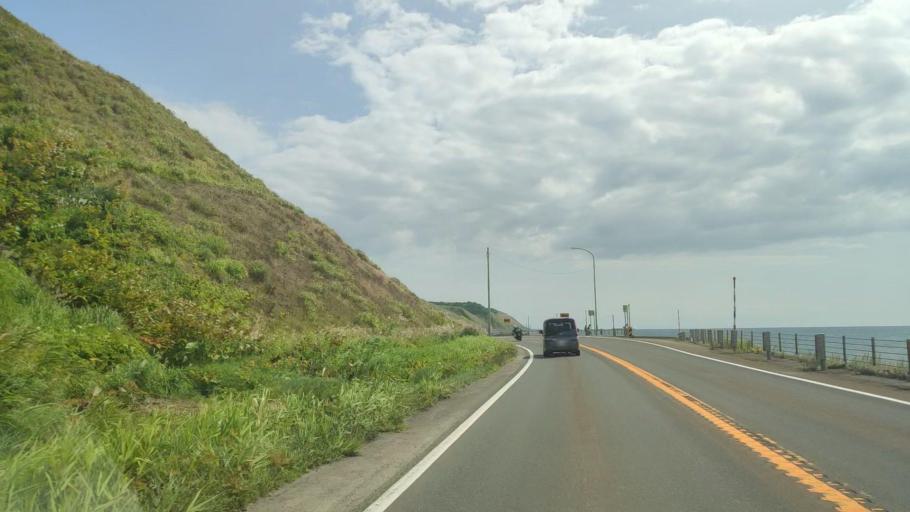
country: JP
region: Hokkaido
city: Rumoi
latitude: 44.2461
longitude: 141.6573
